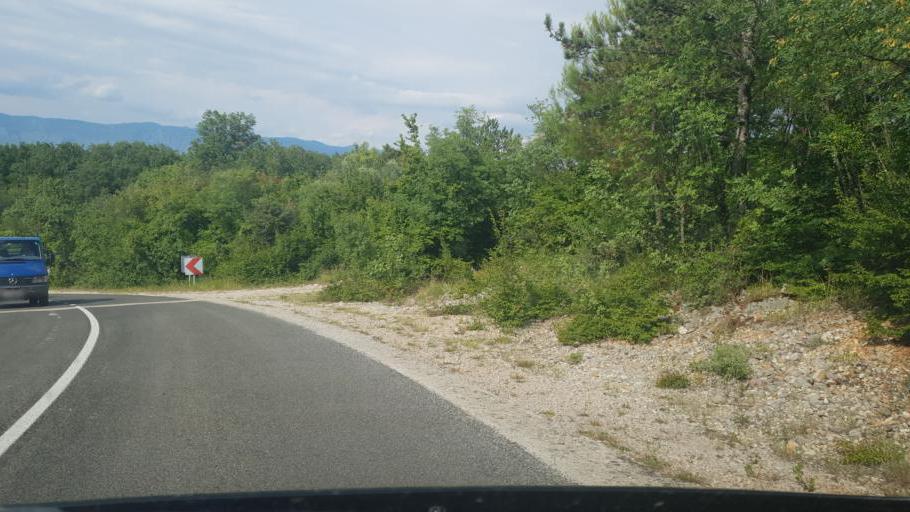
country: HR
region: Primorsko-Goranska
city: Njivice
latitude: 45.1459
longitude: 14.6098
